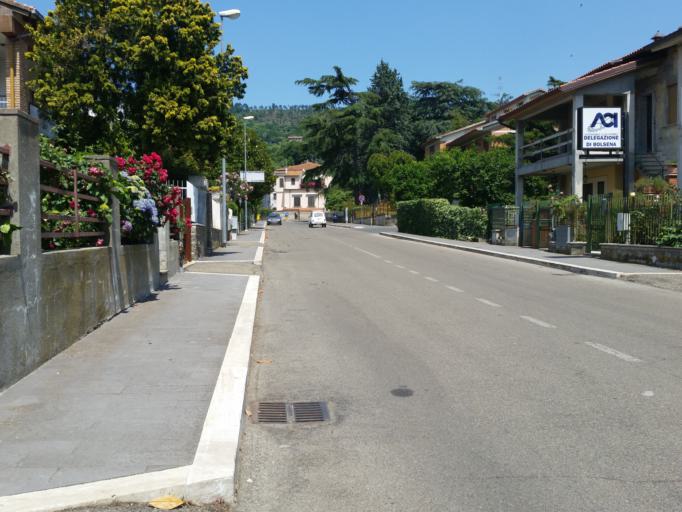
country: IT
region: Latium
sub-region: Provincia di Viterbo
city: Bolsena
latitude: 42.6410
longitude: 11.9880
